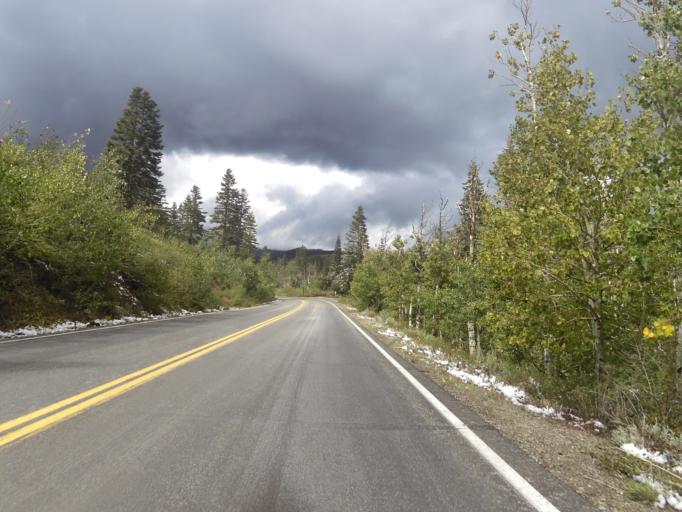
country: US
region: Nevada
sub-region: Douglas County
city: Gardnerville Ranchos
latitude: 38.6648
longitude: -119.6417
